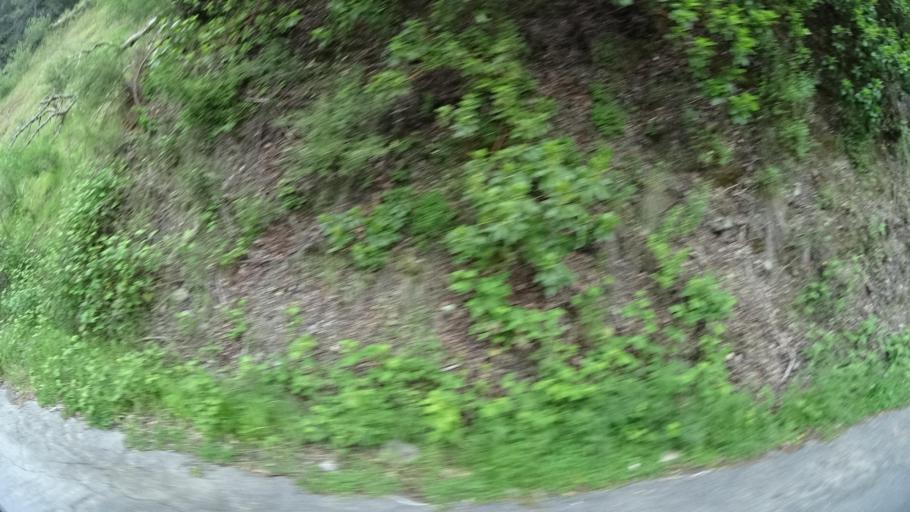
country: US
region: California
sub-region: Humboldt County
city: Willow Creek
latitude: 40.9347
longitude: -123.6158
